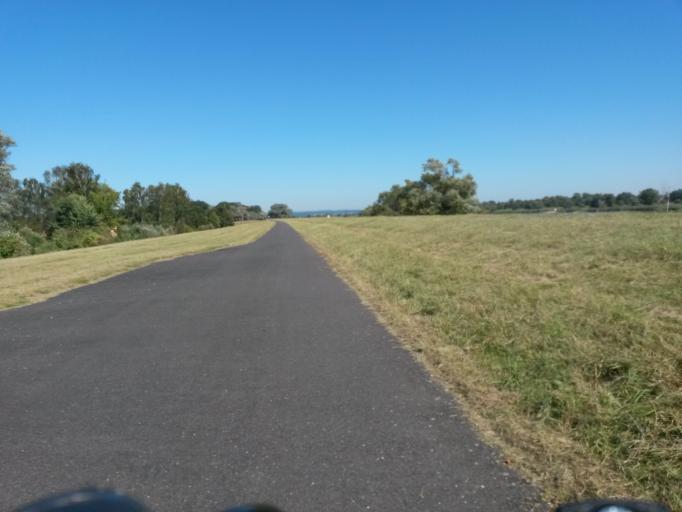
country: PL
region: West Pomeranian Voivodeship
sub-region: Powiat gryfinski
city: Cedynia
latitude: 52.8676
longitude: 14.1448
